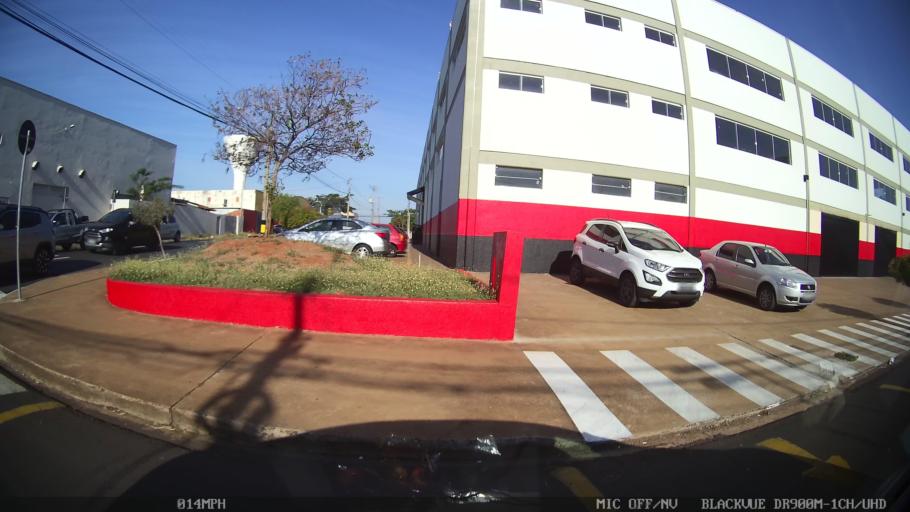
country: BR
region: Sao Paulo
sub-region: Sao Jose Do Rio Preto
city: Sao Jose do Rio Preto
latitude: -20.7909
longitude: -49.3605
